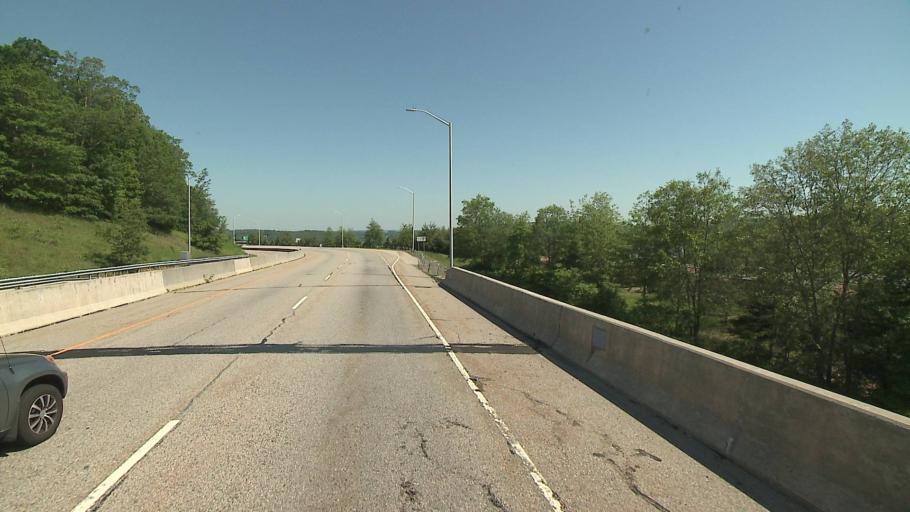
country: US
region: Connecticut
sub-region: New London County
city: Norwich
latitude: 41.4817
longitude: -72.0785
